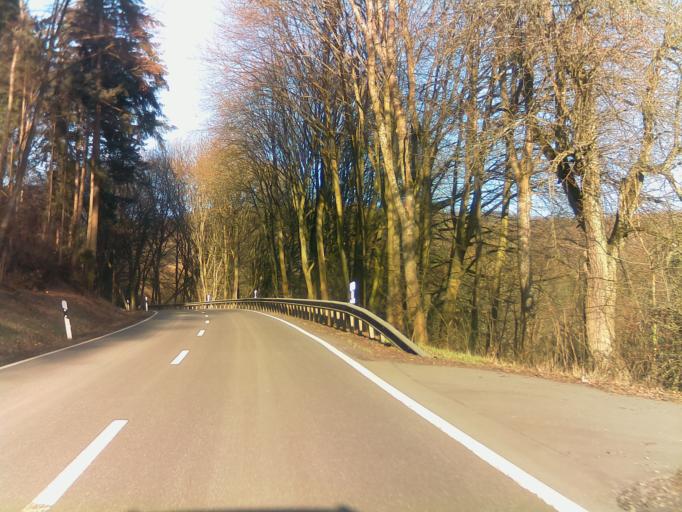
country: DE
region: Rheinland-Pfalz
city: Dannenfels
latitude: 49.6381
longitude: 7.9308
